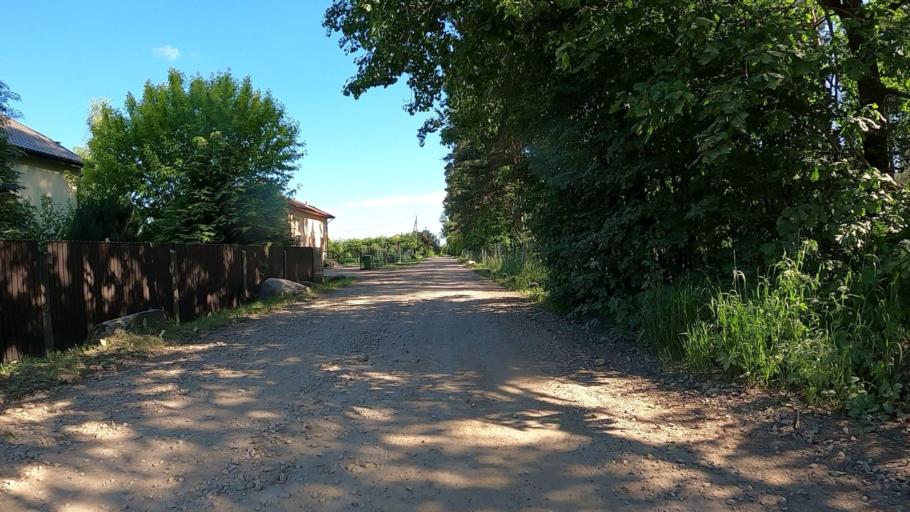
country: LV
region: Stopini
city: Ulbroka
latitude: 56.9089
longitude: 24.3140
